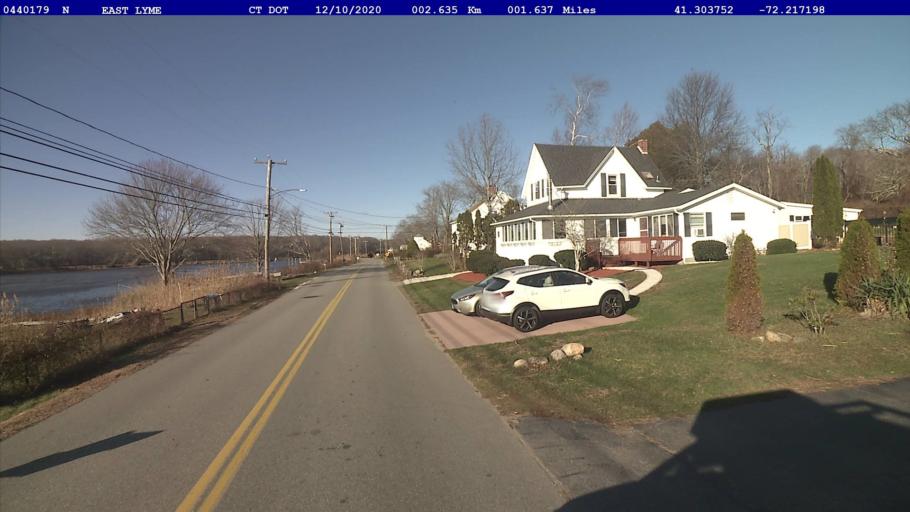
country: US
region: Connecticut
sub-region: New London County
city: Niantic
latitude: 41.3038
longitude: -72.2172
